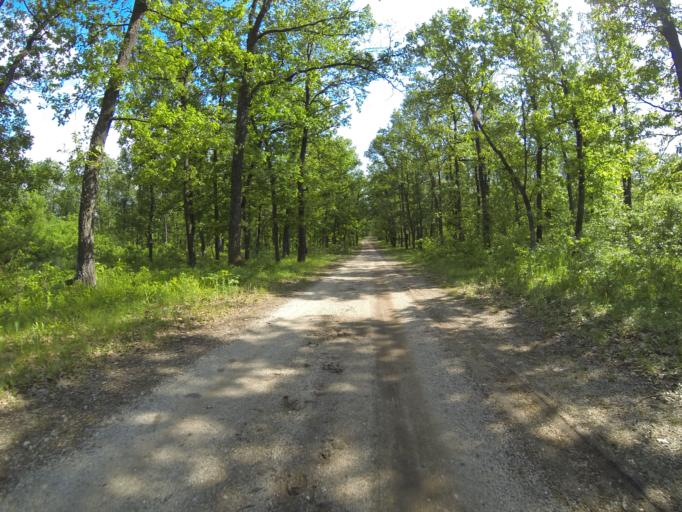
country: RO
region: Dolj
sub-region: Comuna Plenita
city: Castrele Traiane
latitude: 44.2536
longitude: 23.1464
